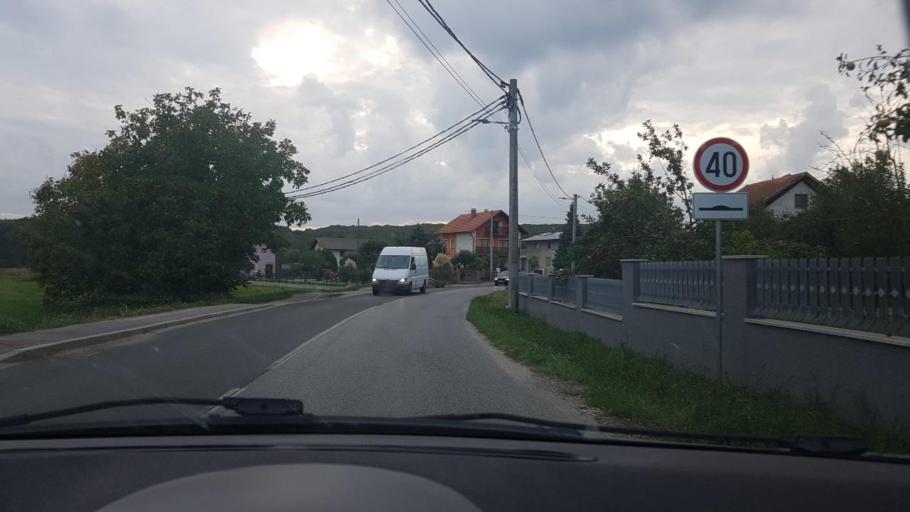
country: HR
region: Grad Zagreb
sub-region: Sesvete
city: Sesvete
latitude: 45.8868
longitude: 16.1746
